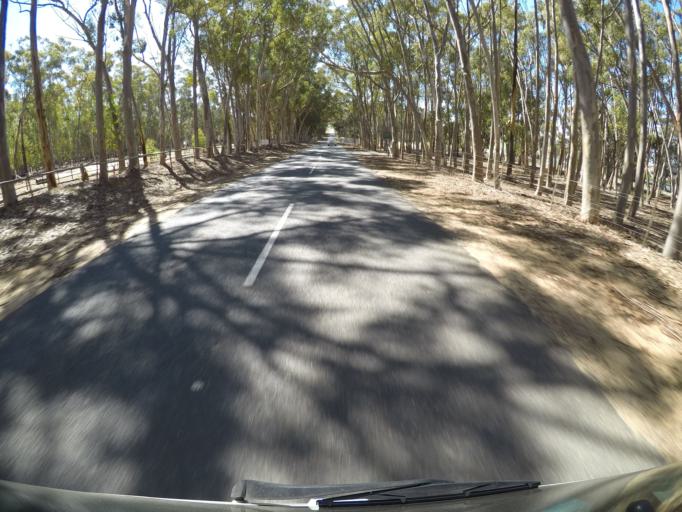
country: ZA
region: Western Cape
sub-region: City of Cape Town
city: Sunset Beach
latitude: -33.7511
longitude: 18.5566
